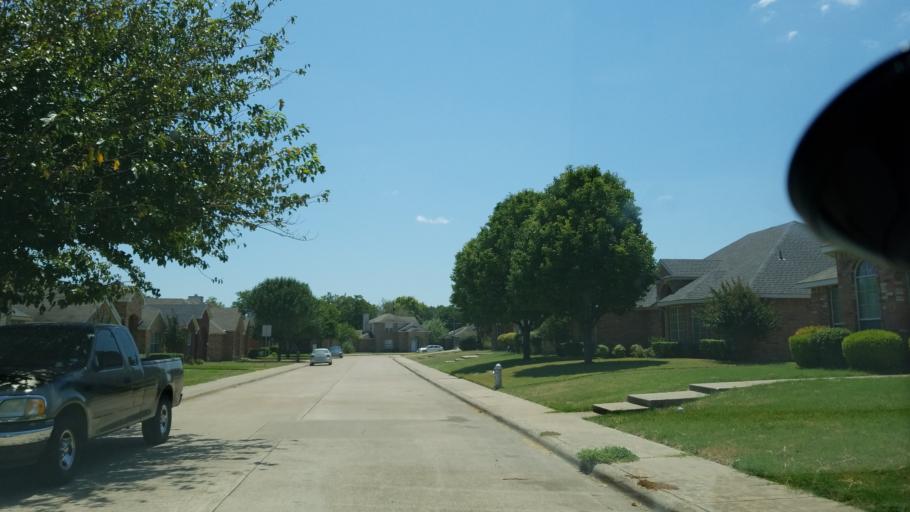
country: US
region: Texas
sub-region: Dallas County
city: Duncanville
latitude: 32.6385
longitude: -96.8841
